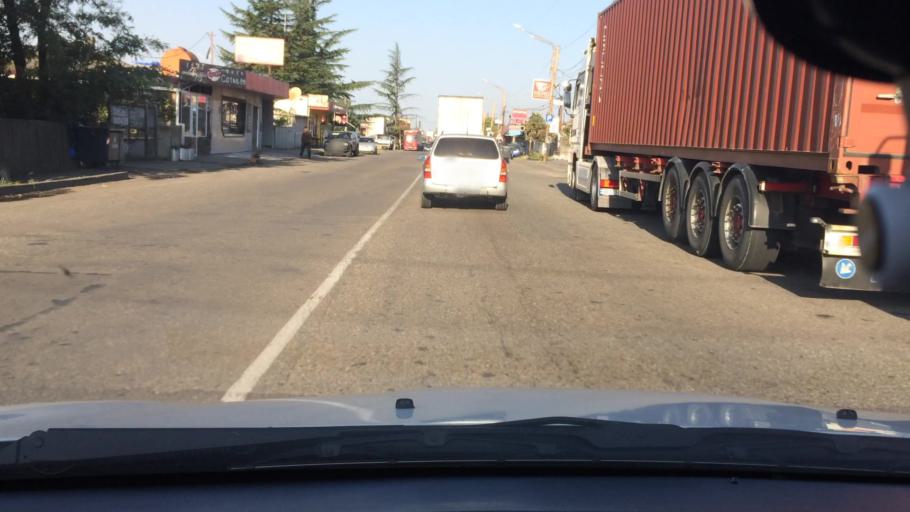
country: GE
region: Imereti
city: Zestap'oni
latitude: 42.1112
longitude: 43.0414
